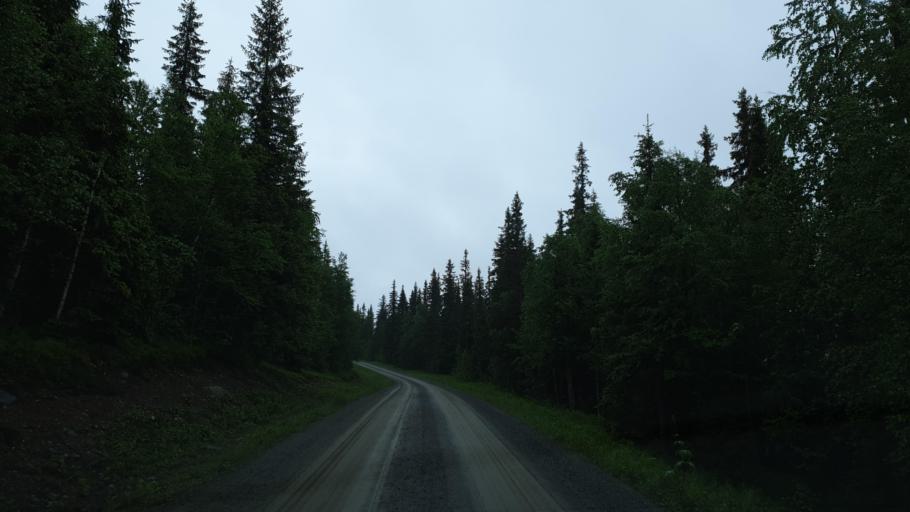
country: SE
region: Vaesterbotten
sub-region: Vilhelmina Kommun
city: Sjoberg
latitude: 65.3313
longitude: 15.9078
